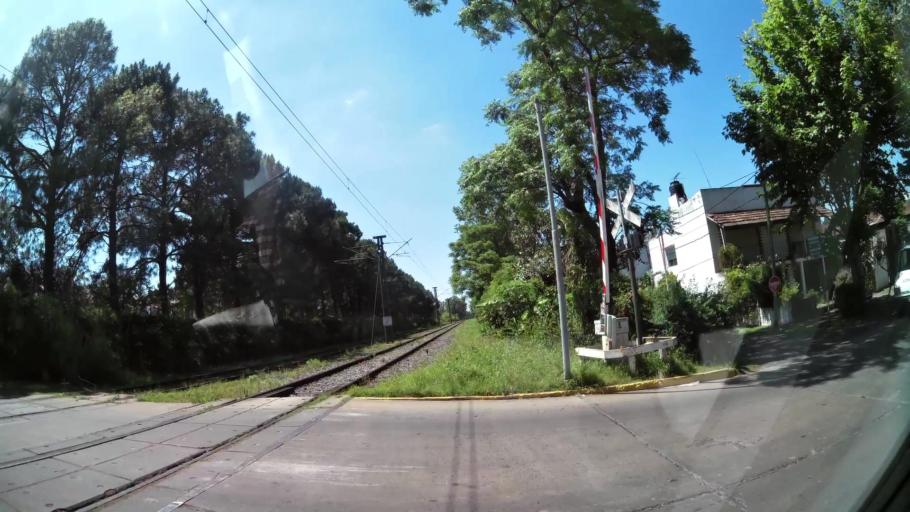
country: AR
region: Buenos Aires
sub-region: Partido de Tigre
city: Tigre
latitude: -34.4242
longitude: -58.5695
